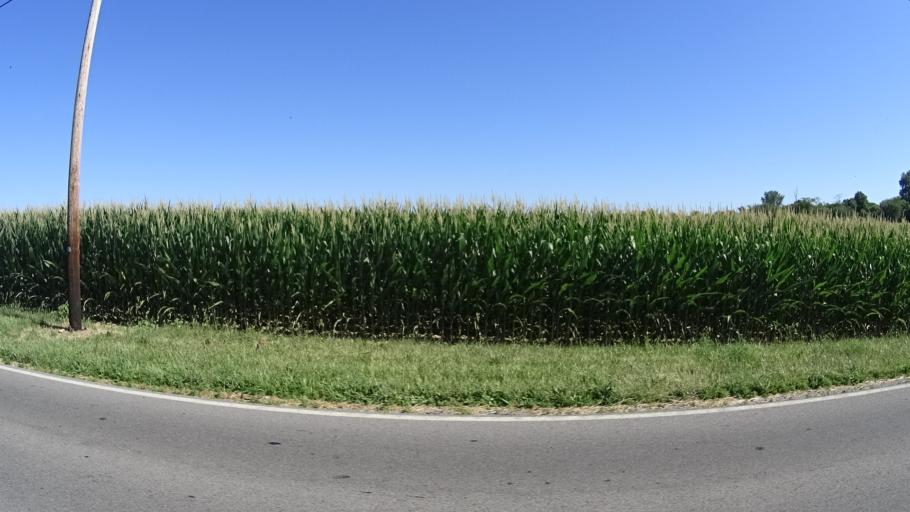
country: US
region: Ohio
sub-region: Erie County
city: Sandusky
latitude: 41.4086
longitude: -82.7079
